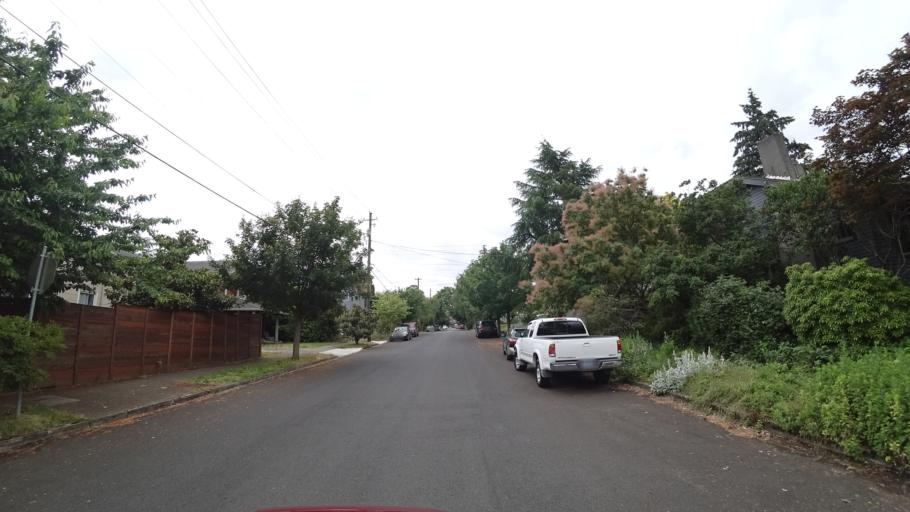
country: US
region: Oregon
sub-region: Multnomah County
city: Portland
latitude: 45.5751
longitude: -122.6728
